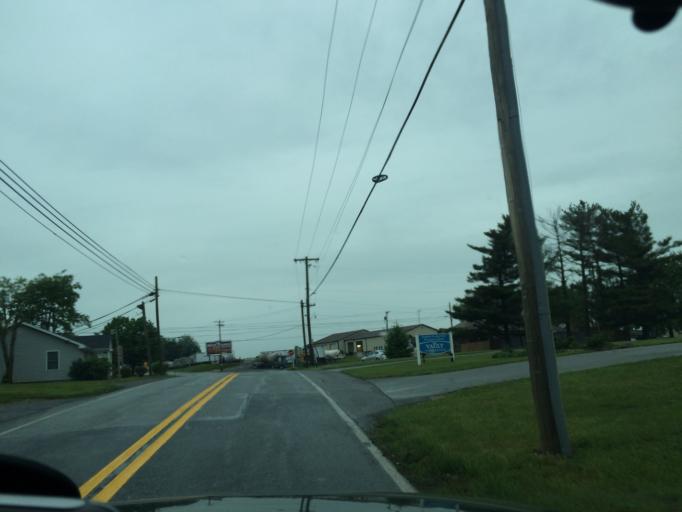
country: US
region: Maryland
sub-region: Carroll County
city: Taneytown
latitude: 39.6025
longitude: -77.2361
